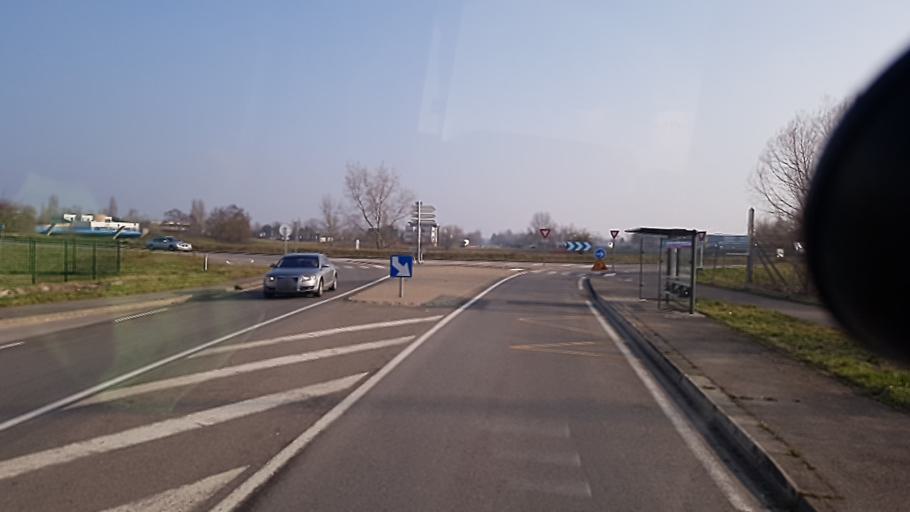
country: FR
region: Alsace
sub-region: Departement du Bas-Rhin
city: Holtzheim
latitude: 48.5418
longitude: 7.6517
